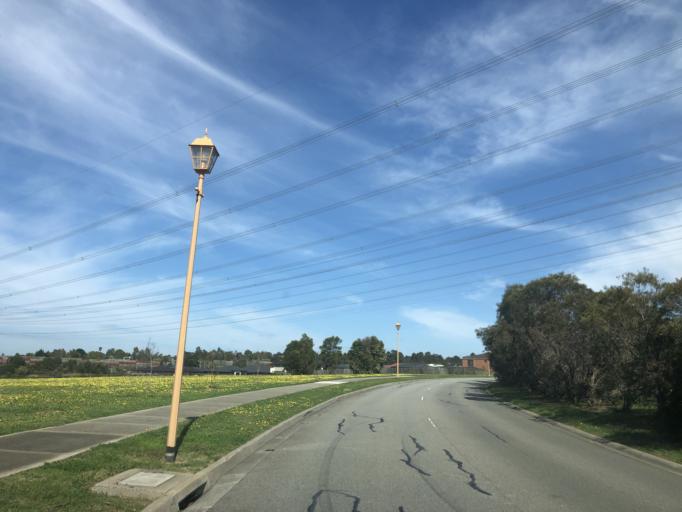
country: AU
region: Victoria
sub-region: Casey
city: Hallam
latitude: -37.9969
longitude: 145.2874
